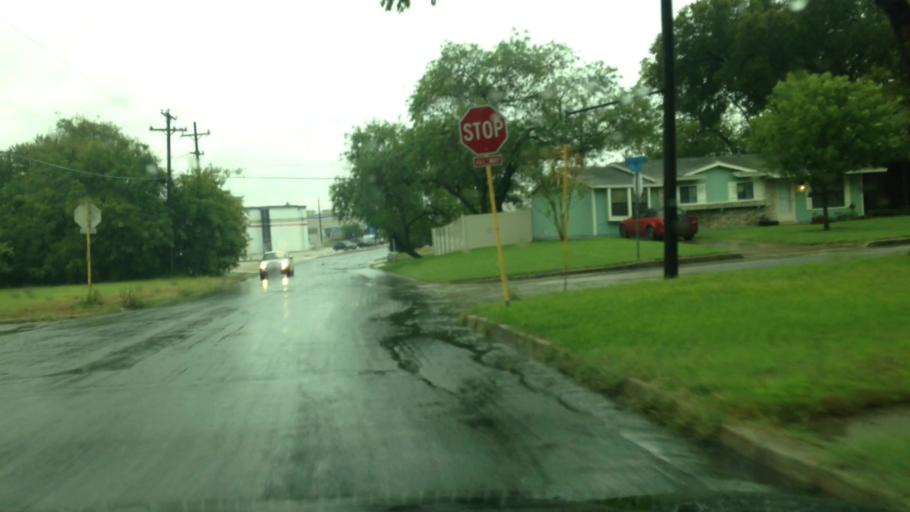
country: US
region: Texas
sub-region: Bexar County
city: Castle Hills
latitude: 29.5142
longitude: -98.5398
